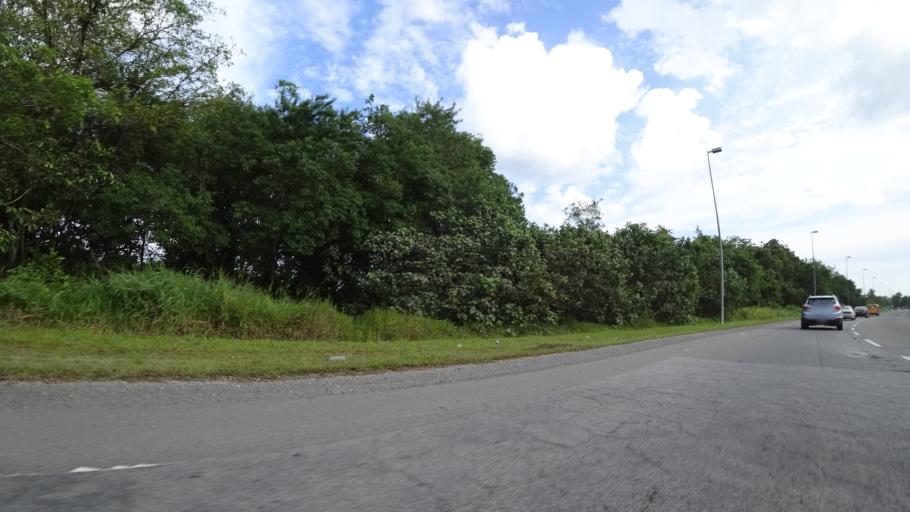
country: BN
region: Brunei and Muara
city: Bandar Seri Begawan
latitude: 4.8159
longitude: 114.8638
